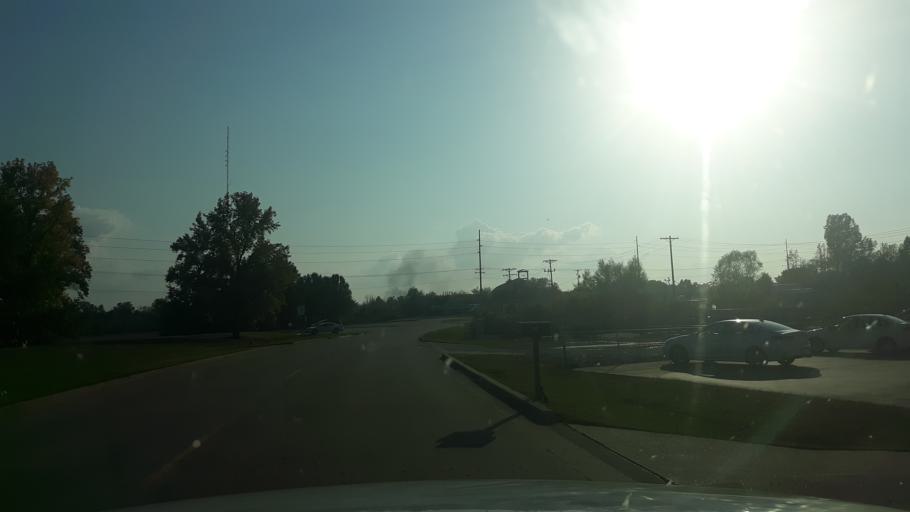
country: US
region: Illinois
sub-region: Saline County
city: Harrisburg
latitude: 37.7215
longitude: -88.5410
